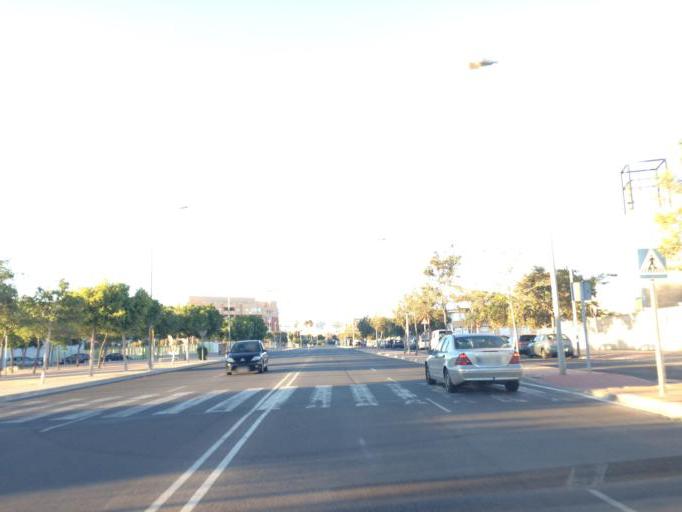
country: ES
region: Andalusia
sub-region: Provincia de Almeria
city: Almeria
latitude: 36.8443
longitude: -2.4329
